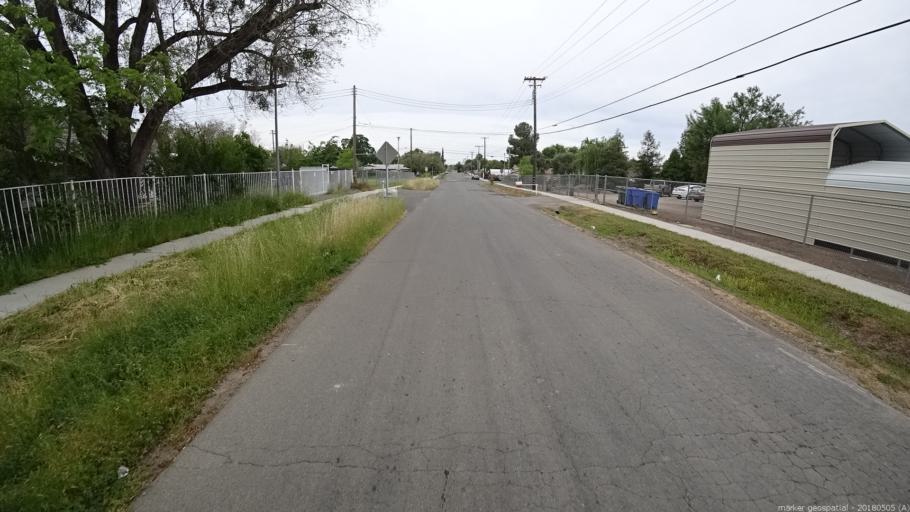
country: US
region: California
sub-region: Sacramento County
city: Rio Linda
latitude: 38.6547
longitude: -121.4374
